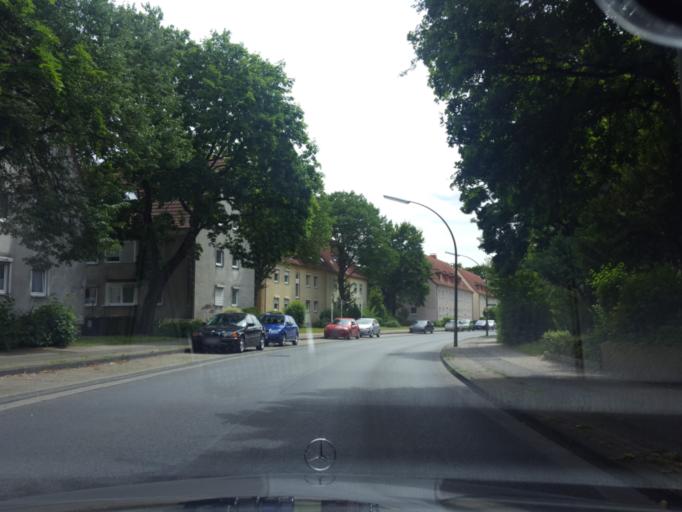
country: DE
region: North Rhine-Westphalia
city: Marl
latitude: 51.6592
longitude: 7.1112
